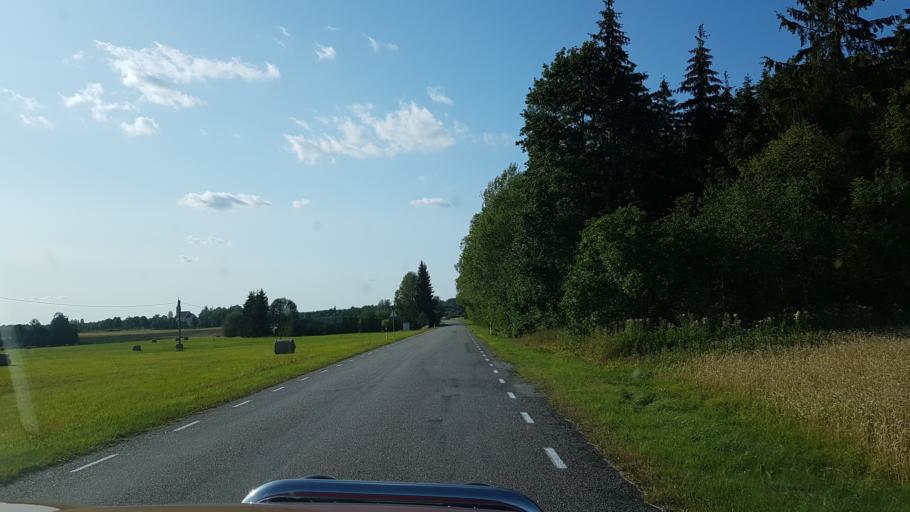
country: EE
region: Jaervamaa
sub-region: Jaerva-Jaani vald
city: Jarva-Jaani
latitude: 59.1118
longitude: 25.6713
